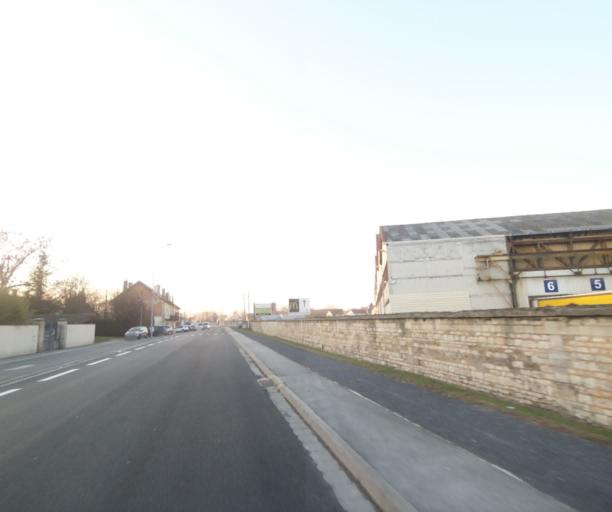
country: FR
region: Champagne-Ardenne
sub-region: Departement de la Haute-Marne
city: Bettancourt-la-Ferree
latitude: 48.6261
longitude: 4.9893
